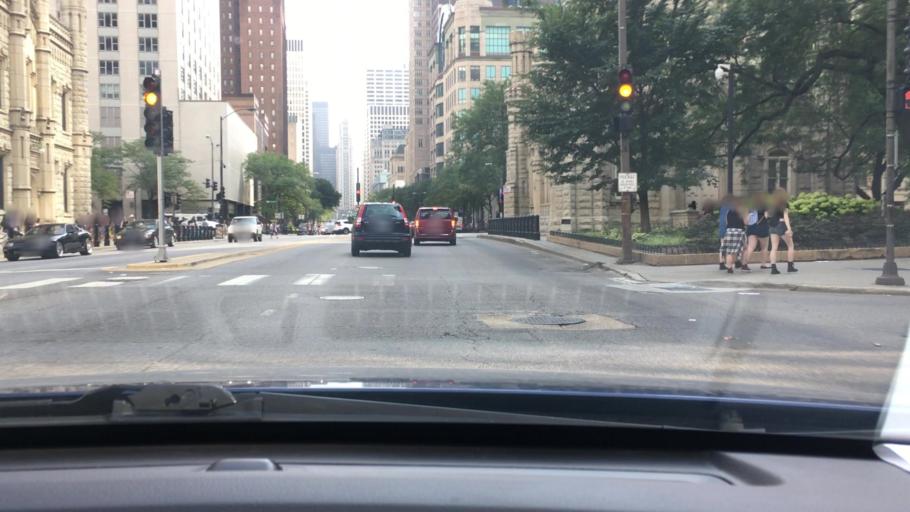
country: US
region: Illinois
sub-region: Cook County
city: Chicago
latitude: 41.8976
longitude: -87.6242
